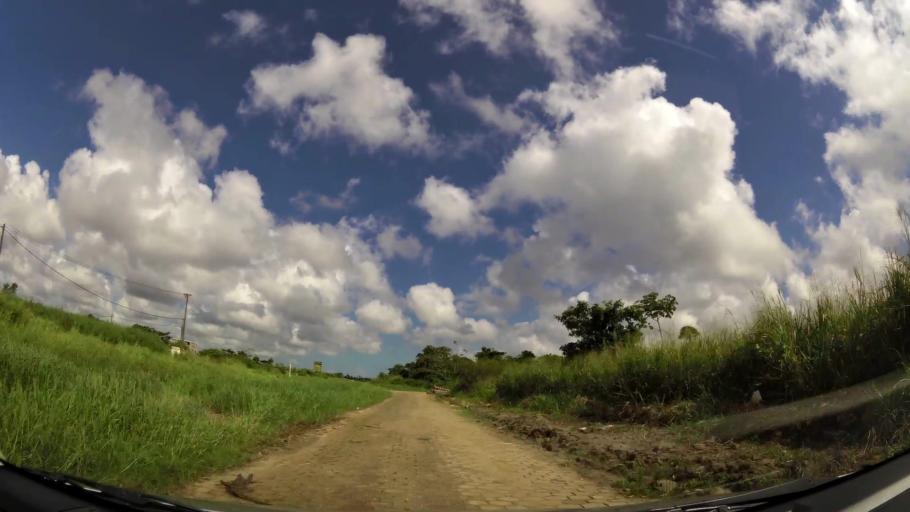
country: SR
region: Paramaribo
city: Paramaribo
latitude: 5.8703
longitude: -55.1268
